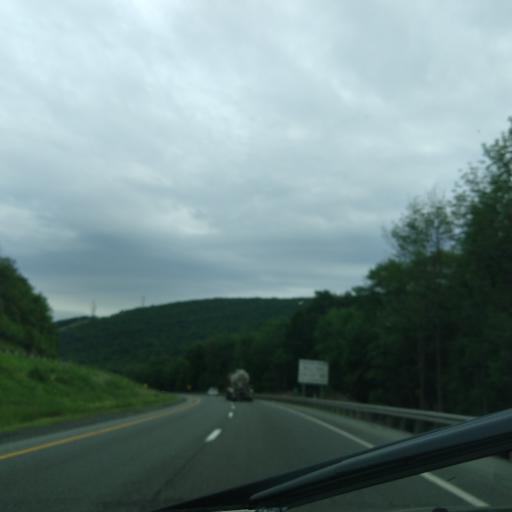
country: US
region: Pennsylvania
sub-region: Lackawanna County
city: Chinchilla
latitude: 41.4772
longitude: -75.6822
